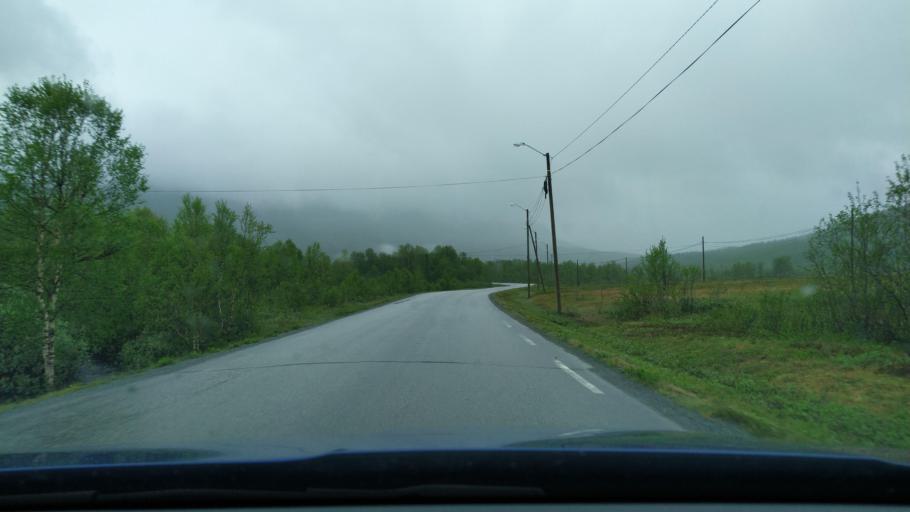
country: NO
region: Troms
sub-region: Dyroy
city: Brostadbotn
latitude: 69.0381
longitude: 17.7332
